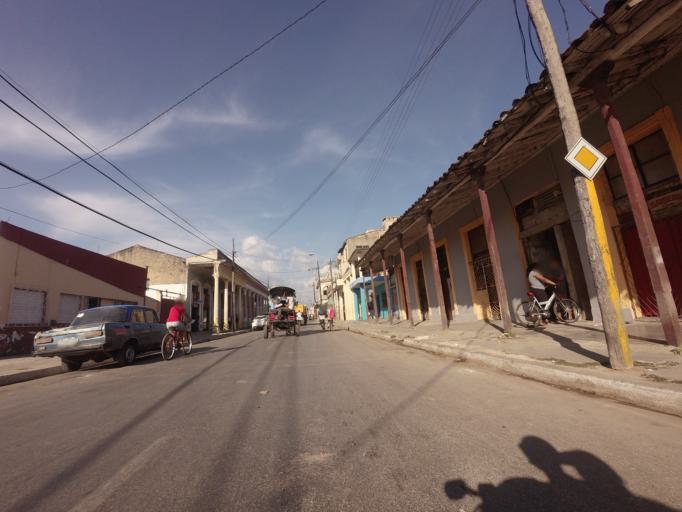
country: CU
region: Ciego de Avila
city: Ciego de Avila
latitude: 21.8413
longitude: -78.7637
